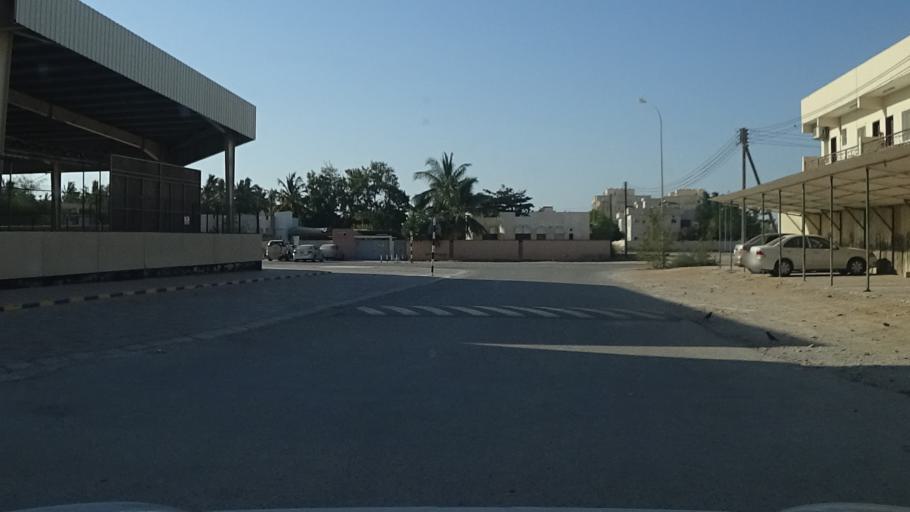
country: OM
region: Zufar
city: Salalah
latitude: 17.0318
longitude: 54.1598
